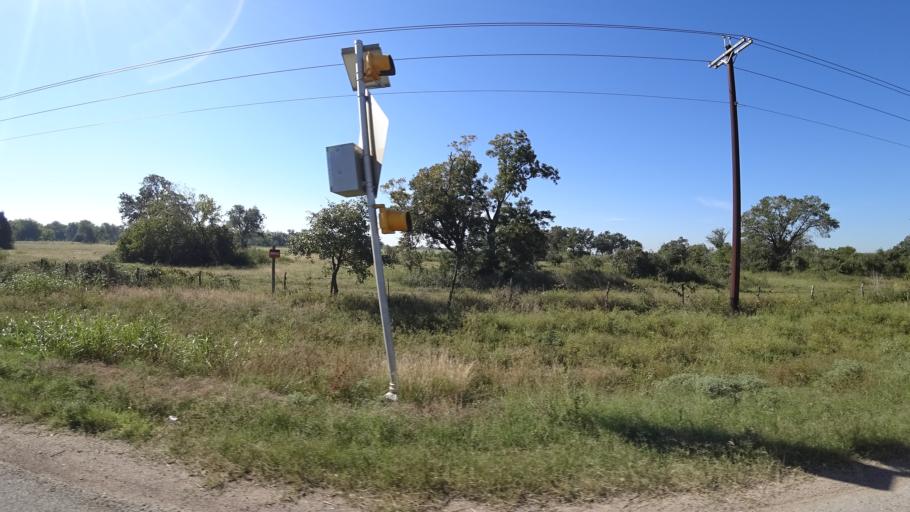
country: US
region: Texas
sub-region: Travis County
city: Hornsby Bend
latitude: 30.2507
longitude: -97.5921
